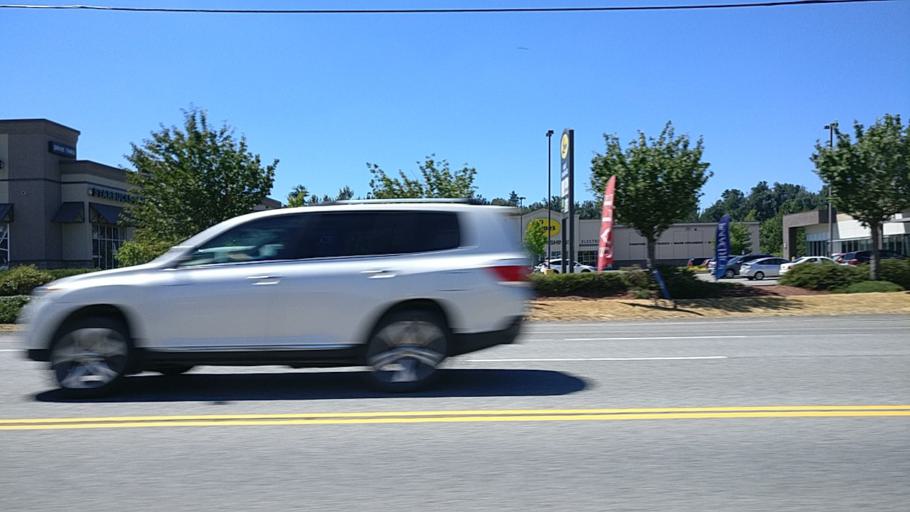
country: US
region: Washington
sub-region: Whatcom County
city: Sumas
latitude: 49.0281
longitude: -122.2654
